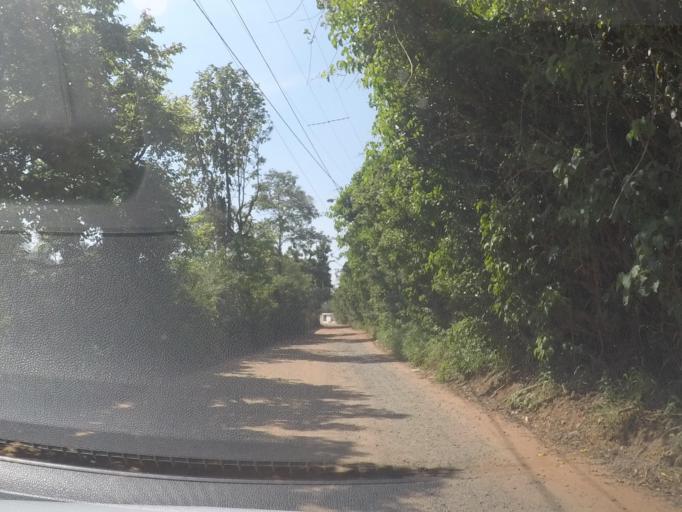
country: BR
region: Sao Paulo
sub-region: Monte Mor
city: Monte Mor
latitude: -22.8850
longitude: -47.3026
